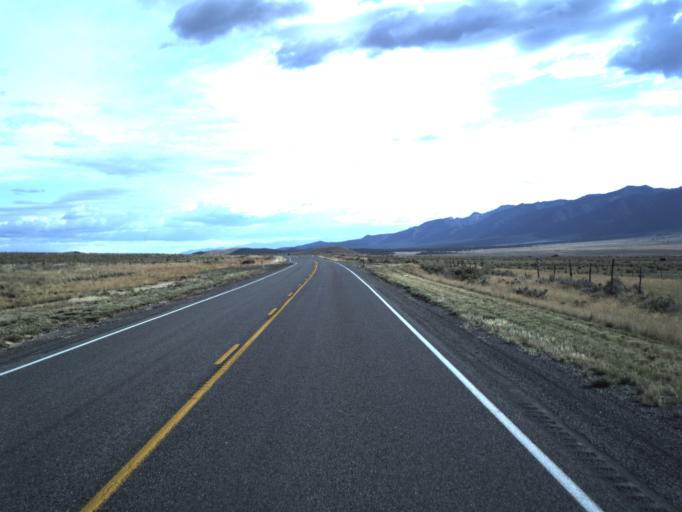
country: US
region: Utah
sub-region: Sevier County
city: Aurora
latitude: 39.0448
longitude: -112.0420
